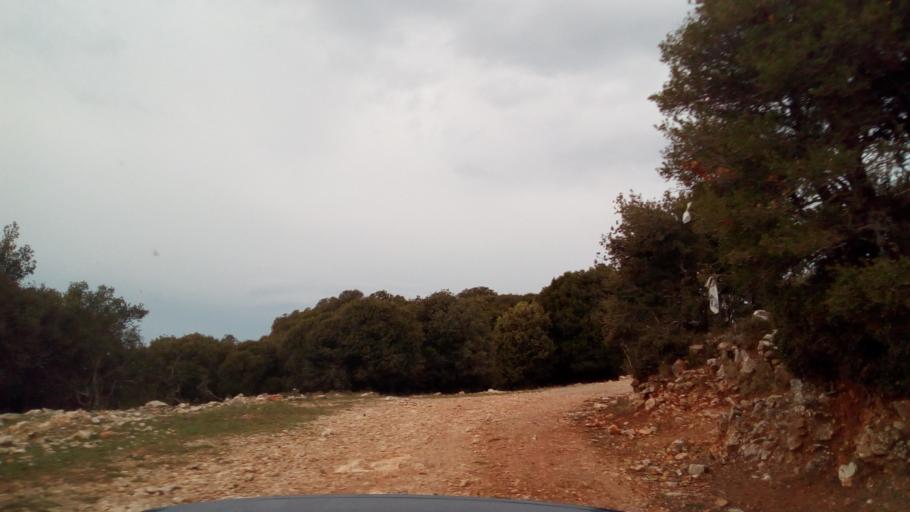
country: GR
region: West Greece
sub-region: Nomos Achaias
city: Kamarai
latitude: 38.4146
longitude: 22.0385
